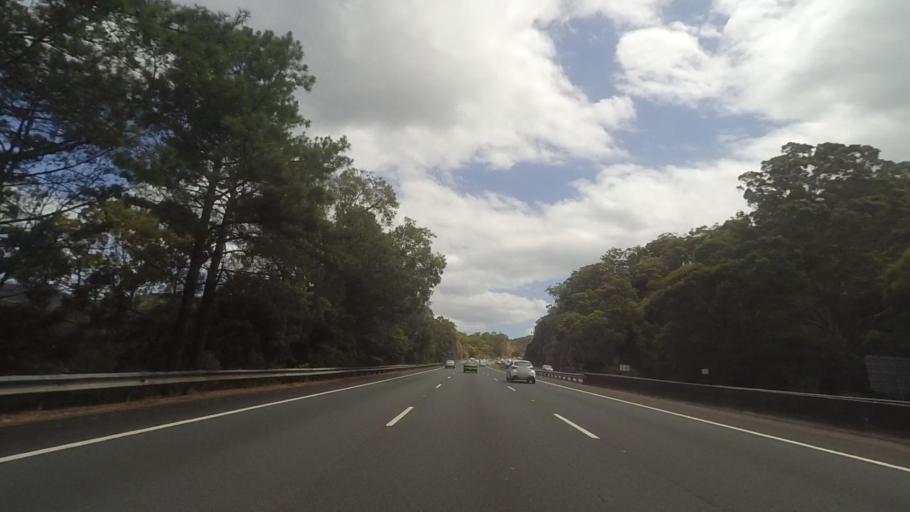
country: AU
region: New South Wales
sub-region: Hornsby Shire
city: Berowra
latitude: -33.5434
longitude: 151.1976
